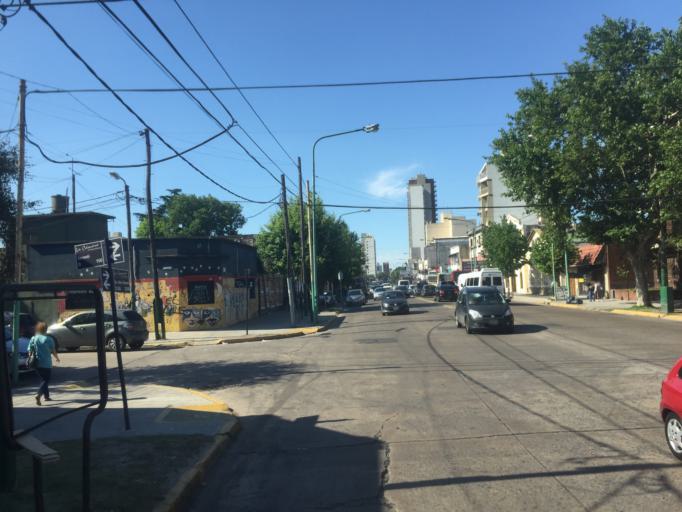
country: AR
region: Buenos Aires
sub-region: Partido de Lomas de Zamora
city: Lomas de Zamora
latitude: -34.7625
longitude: -58.3965
